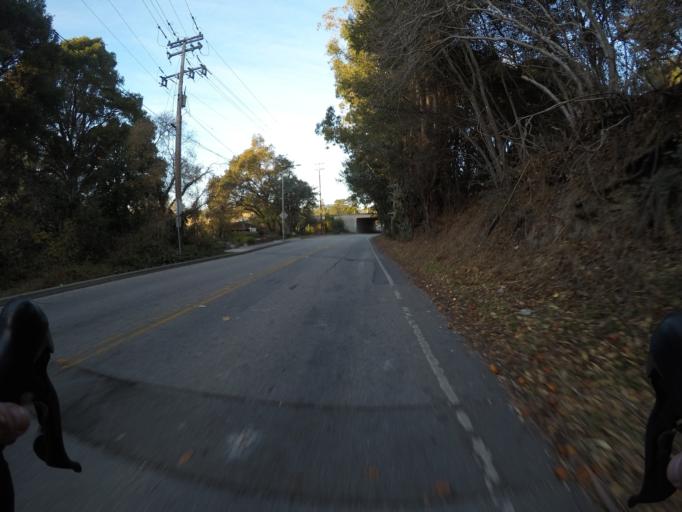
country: US
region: California
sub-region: Santa Cruz County
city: Pasatiempo
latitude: 36.9875
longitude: -122.0135
